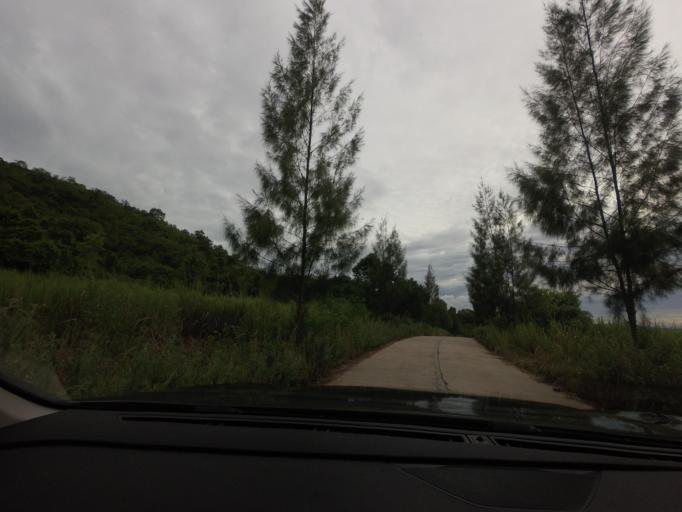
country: TH
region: Prachuap Khiri Khan
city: Hua Hin
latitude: 12.4835
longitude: 99.9429
